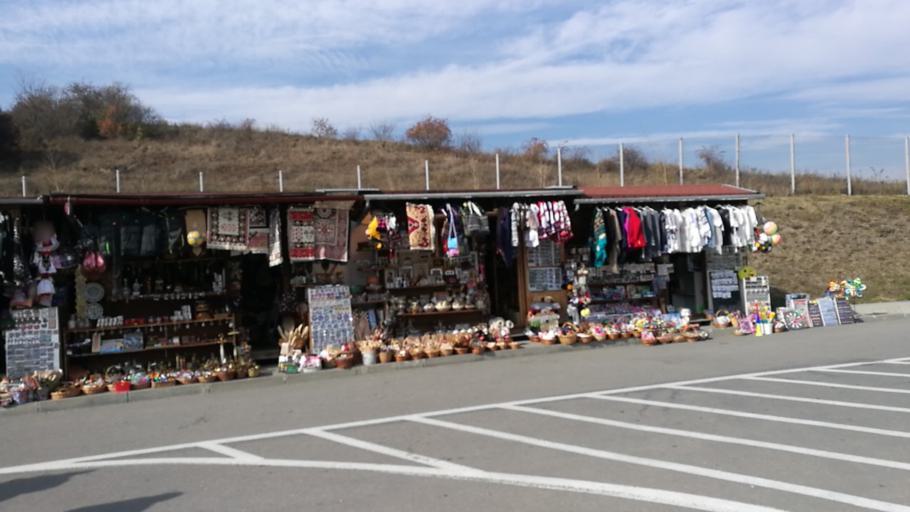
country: RO
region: Cluj
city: Turda
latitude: 46.5886
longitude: 23.7874
